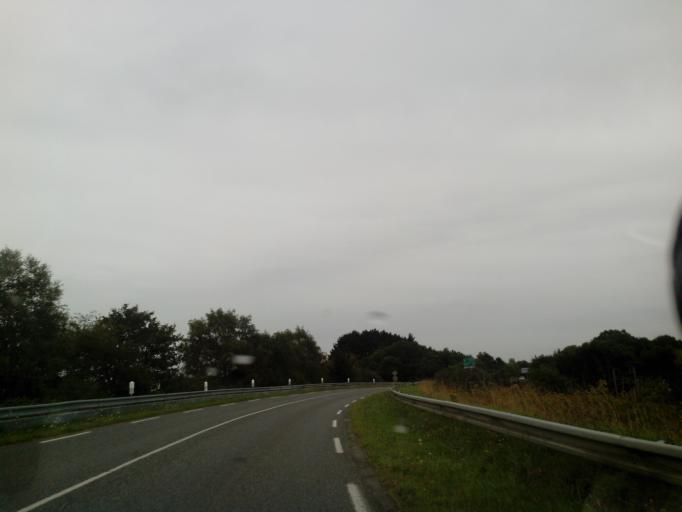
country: FR
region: Brittany
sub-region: Departement du Finistere
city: Redene
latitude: 47.8511
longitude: -3.5092
